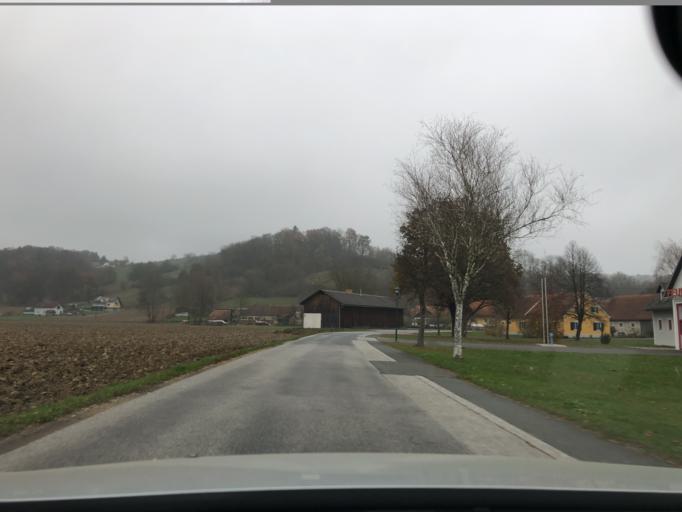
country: AT
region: Styria
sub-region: Politischer Bezirk Suedoststeiermark
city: Fehring
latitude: 46.9532
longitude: 16.0340
